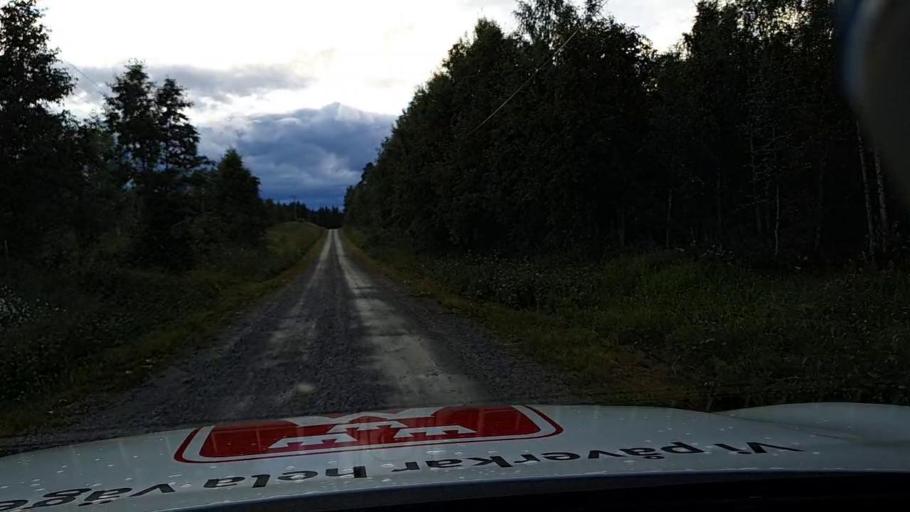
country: SE
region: Jaemtland
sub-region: Bergs Kommun
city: Hoverberg
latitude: 62.8729
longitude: 14.6200
